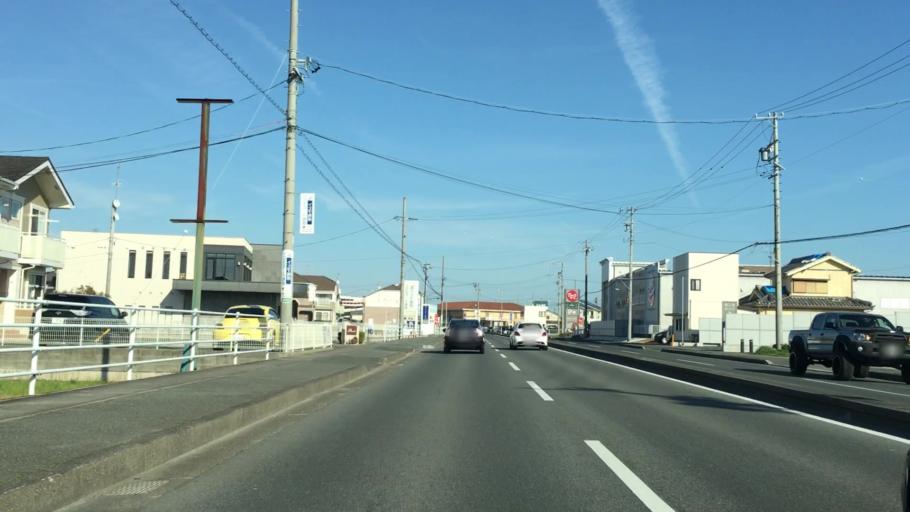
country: JP
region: Shizuoka
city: Hamamatsu
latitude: 34.6958
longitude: 137.6385
